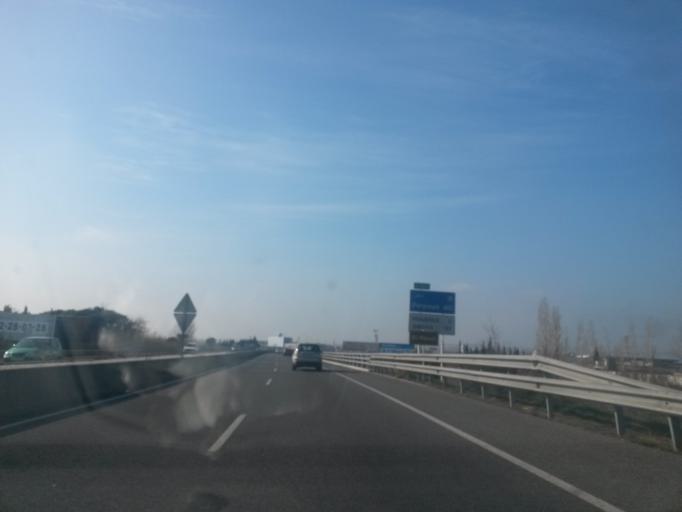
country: ES
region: Catalonia
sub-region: Provincia de Girona
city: Vila-sacra
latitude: 42.2685
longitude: 3.0060
